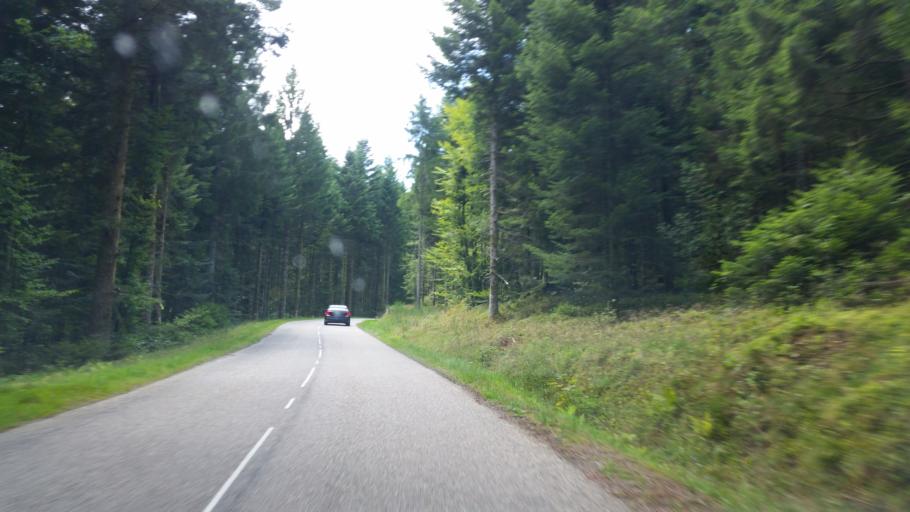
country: FR
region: Lorraine
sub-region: Departement des Vosges
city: Granges-sur-Vologne
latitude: 48.0974
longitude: 6.7974
